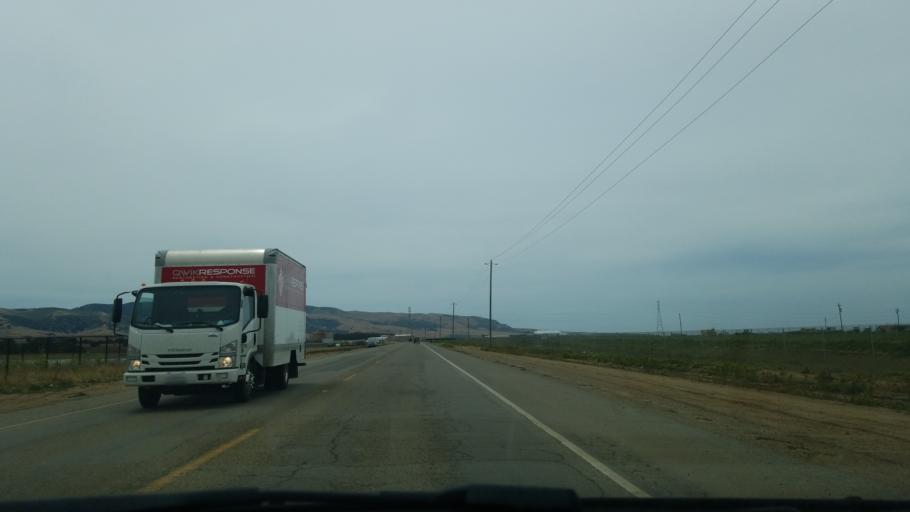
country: US
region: California
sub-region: Santa Barbara County
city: Santa Maria
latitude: 34.9206
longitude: -120.4951
